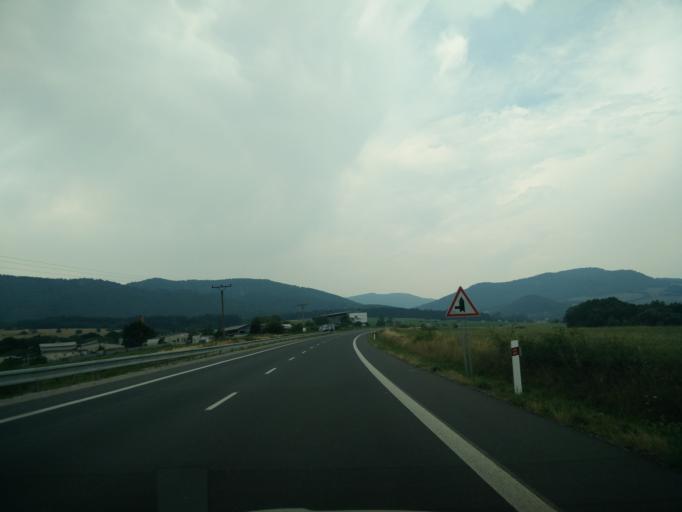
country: SK
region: Banskobystricky
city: Ziar nad Hronom
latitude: 48.6275
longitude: 18.7838
